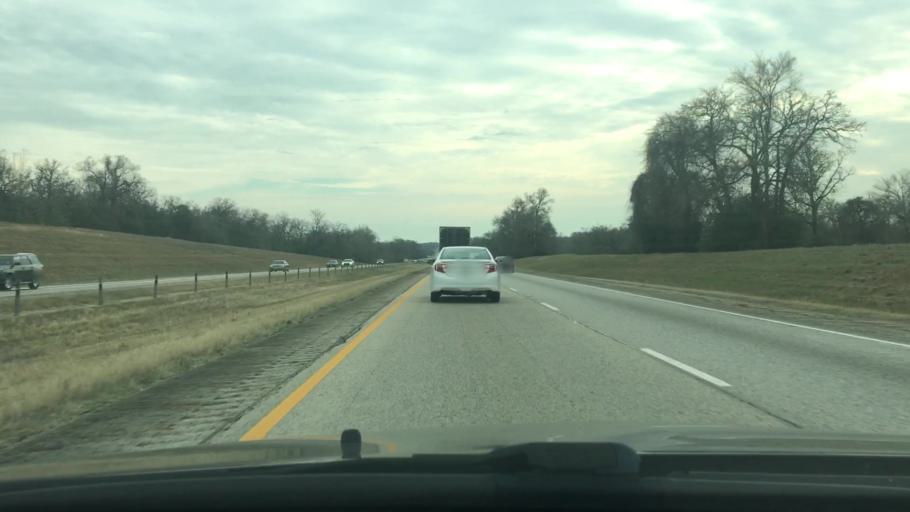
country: US
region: Texas
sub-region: Leon County
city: Centerville
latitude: 31.2022
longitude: -95.9951
